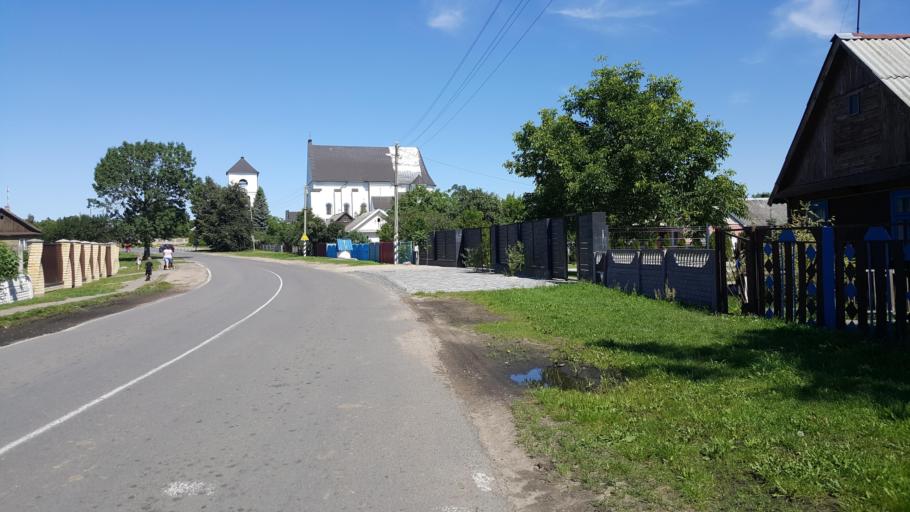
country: BY
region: Brest
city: Charnawchytsy
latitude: 52.2165
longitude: 23.7409
